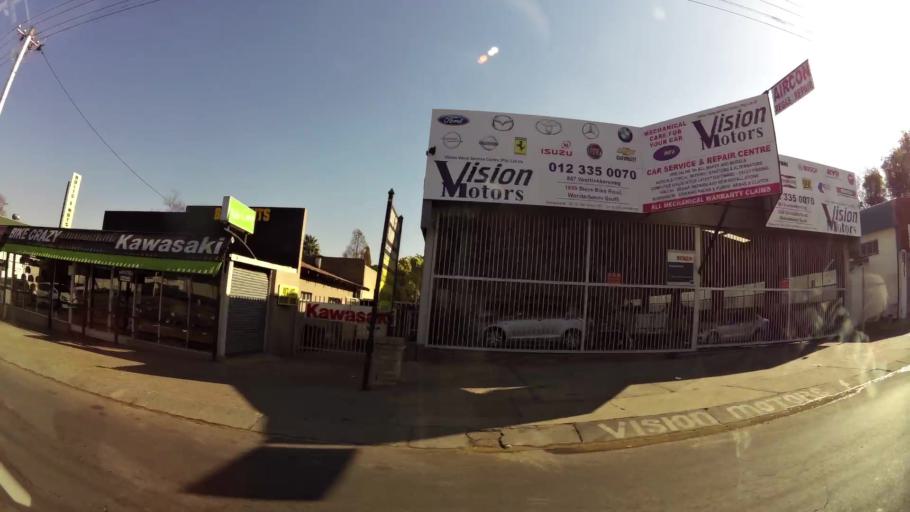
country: ZA
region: Gauteng
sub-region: City of Tshwane Metropolitan Municipality
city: Pretoria
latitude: -25.7023
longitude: 28.1999
